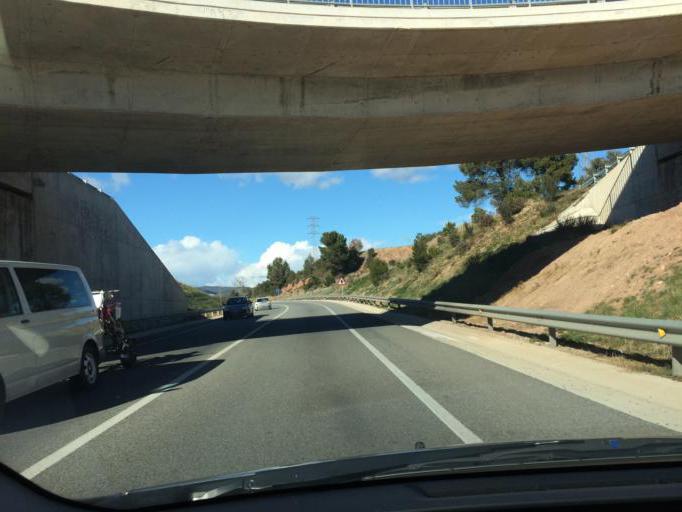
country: ES
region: Catalonia
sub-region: Provincia de Barcelona
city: Sant Joan de Vilatorrada
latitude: 41.7562
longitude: 1.7981
